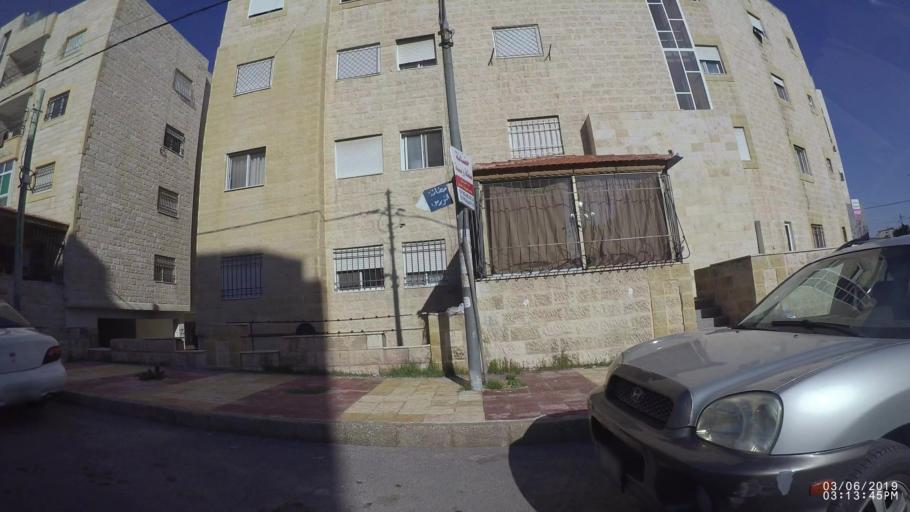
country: JO
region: Amman
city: Amman
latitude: 31.9798
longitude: 35.9343
